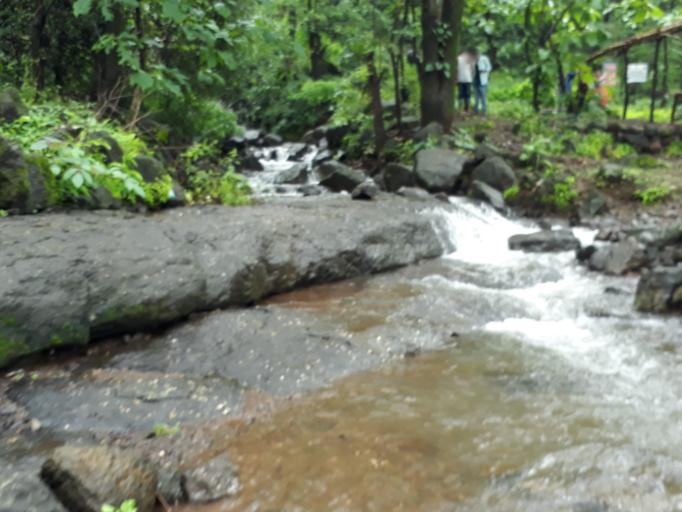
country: IN
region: Maharashtra
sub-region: Raigarh
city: Khopoli
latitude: 18.8399
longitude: 73.3837
